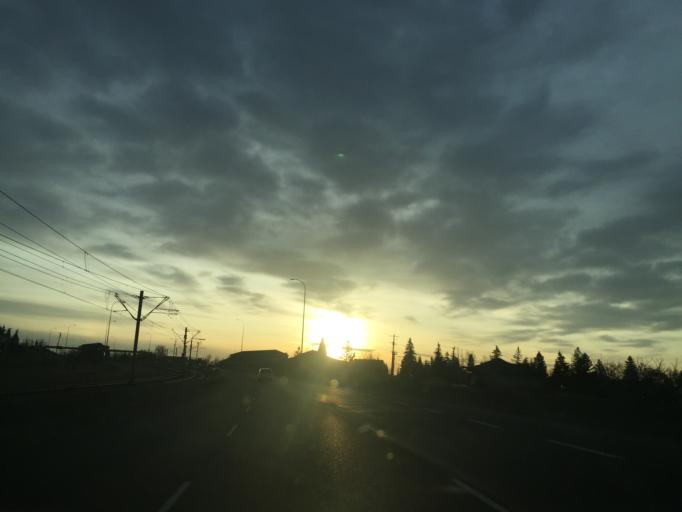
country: CA
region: Alberta
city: Calgary
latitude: 51.0451
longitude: -114.0008
